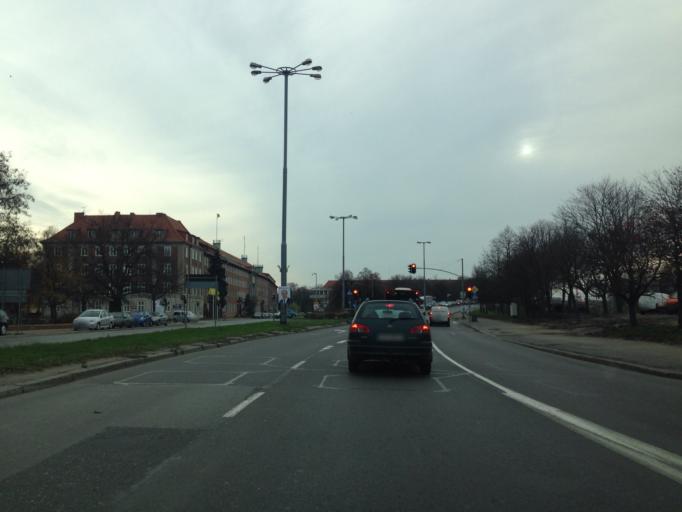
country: PL
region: Pomeranian Voivodeship
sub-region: Gdansk
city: Gdansk
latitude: 54.3461
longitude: 18.6453
